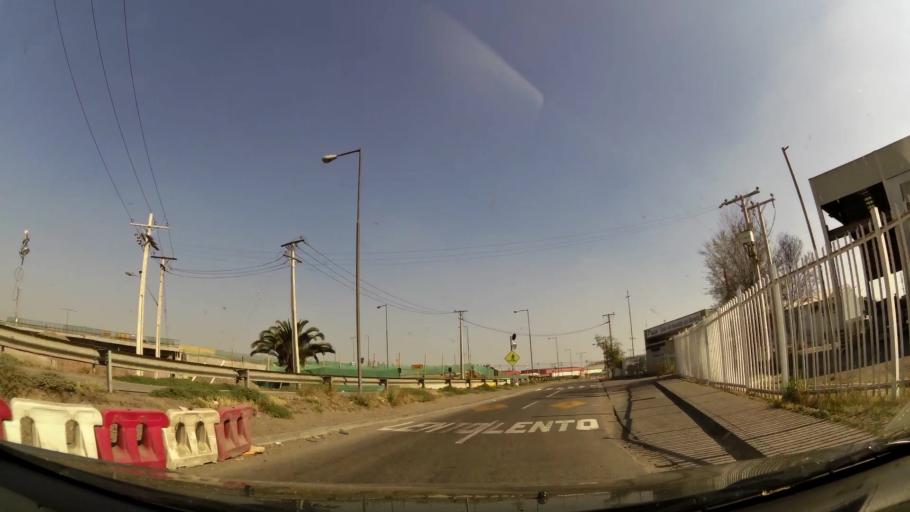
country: CL
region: Santiago Metropolitan
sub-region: Provincia de Chacabuco
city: Chicureo Abajo
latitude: -33.3332
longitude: -70.7156
